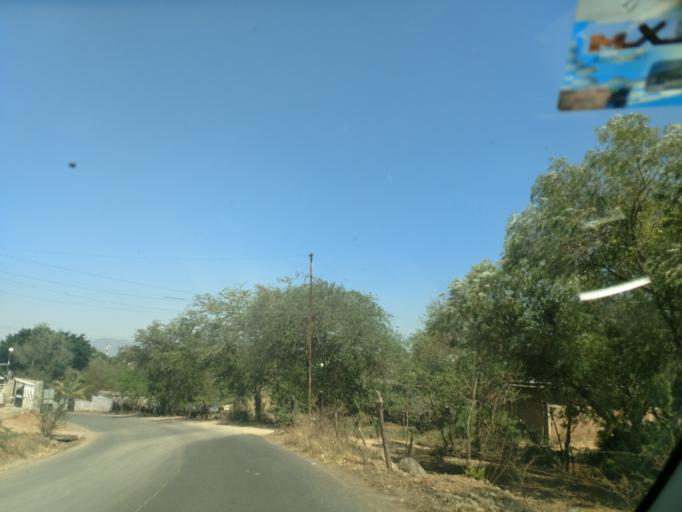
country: MX
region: Nayarit
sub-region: Tepic
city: La Corregidora
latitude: 21.4696
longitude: -104.6605
